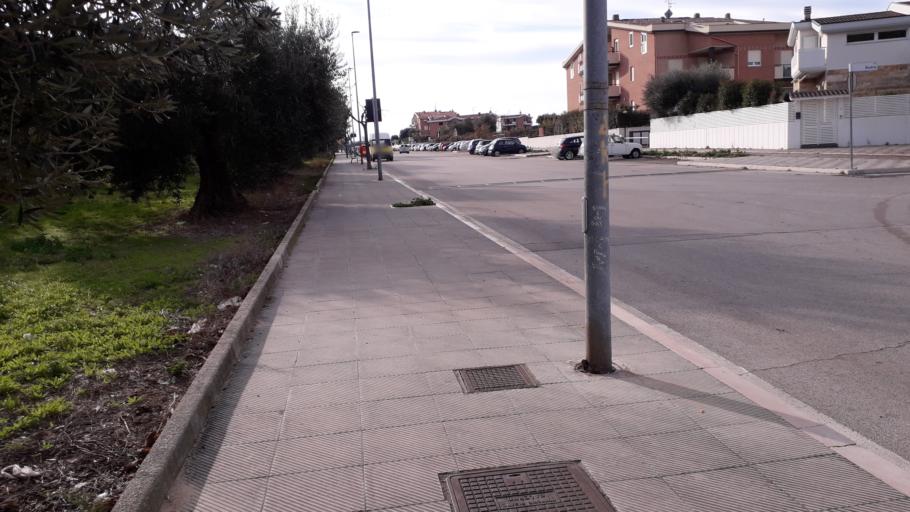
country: IT
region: Molise
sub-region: Provincia di Campobasso
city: Campomarino
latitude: 41.9535
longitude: 15.0319
